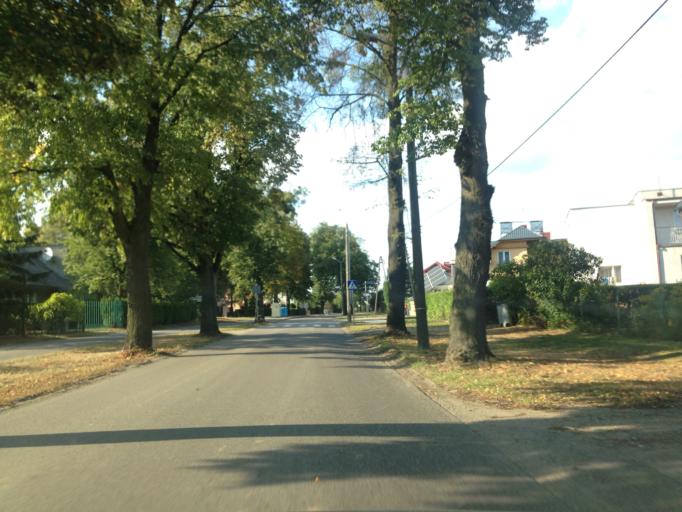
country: PL
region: Warmian-Masurian Voivodeship
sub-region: Powiat ilawski
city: Ilawa
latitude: 53.6148
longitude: 19.5685
